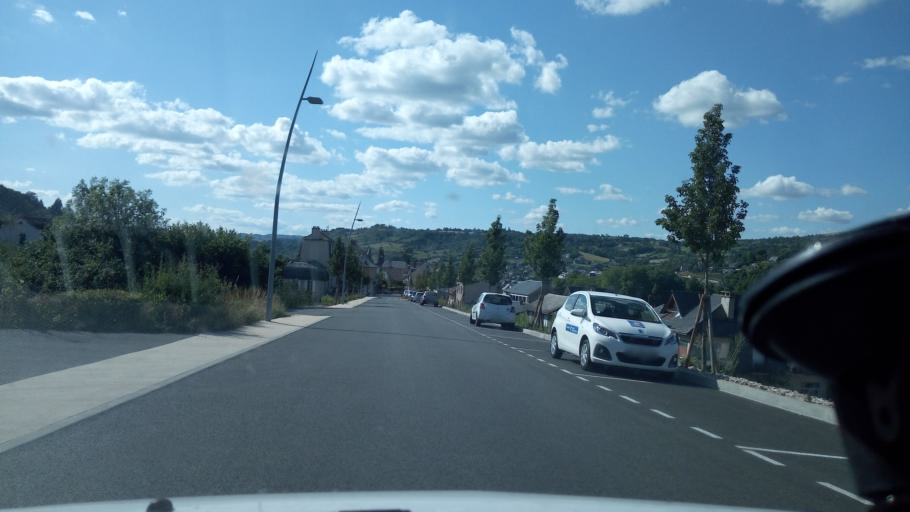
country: FR
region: Midi-Pyrenees
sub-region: Departement de l'Aveyron
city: Espalion
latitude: 44.5172
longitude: 2.7677
